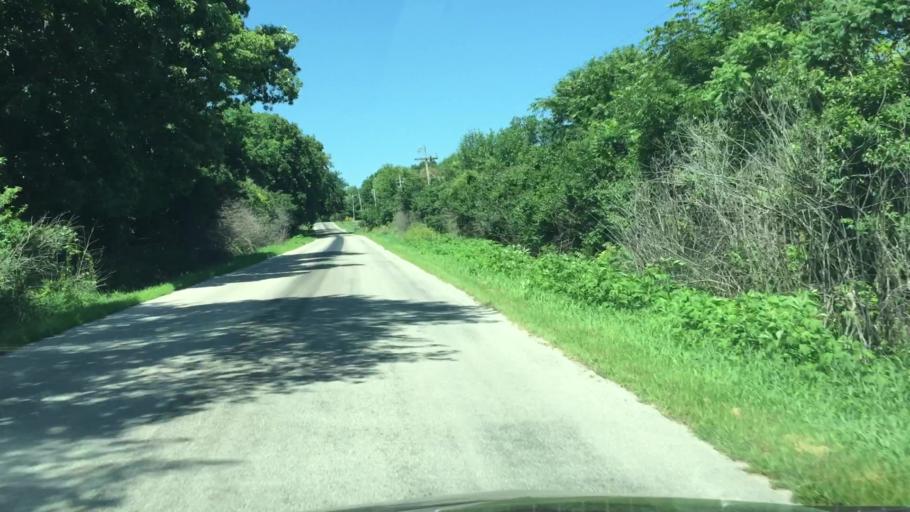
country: US
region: Iowa
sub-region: Linn County
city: Ely
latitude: 41.8148
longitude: -91.5962
